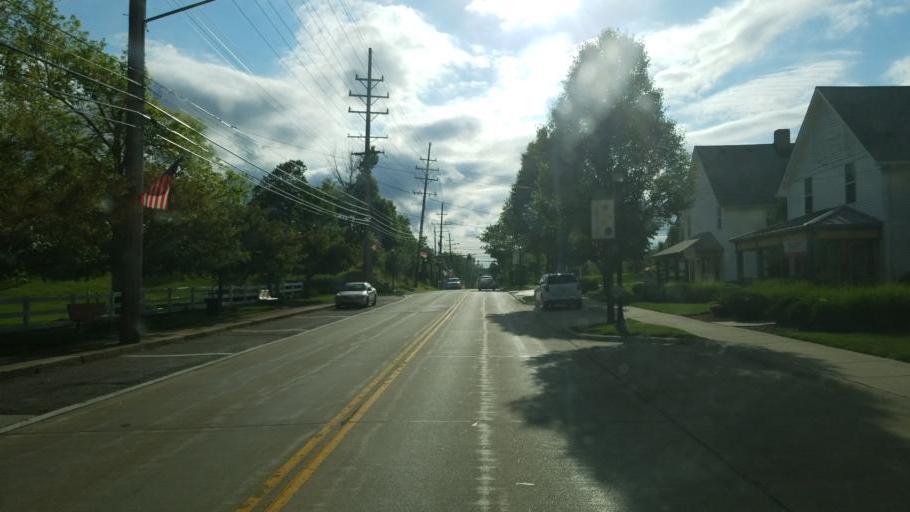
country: US
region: Ohio
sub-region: Cuyahoga County
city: Oakwood
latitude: 41.3569
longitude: -81.4683
